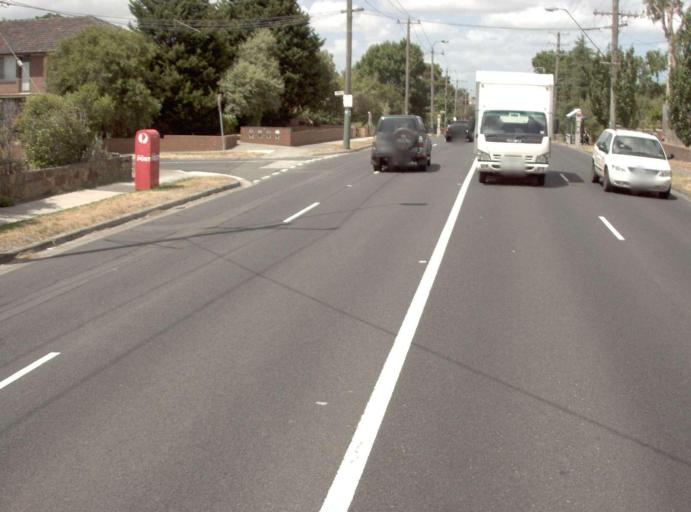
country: AU
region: Victoria
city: Ashburton
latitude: -37.8596
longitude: 145.0940
